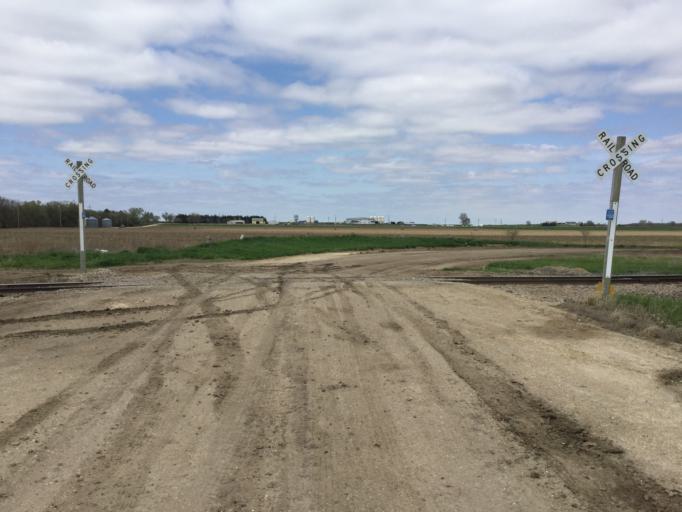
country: US
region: Kansas
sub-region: Osborne County
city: Osborne
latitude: 39.5026
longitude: -98.5336
